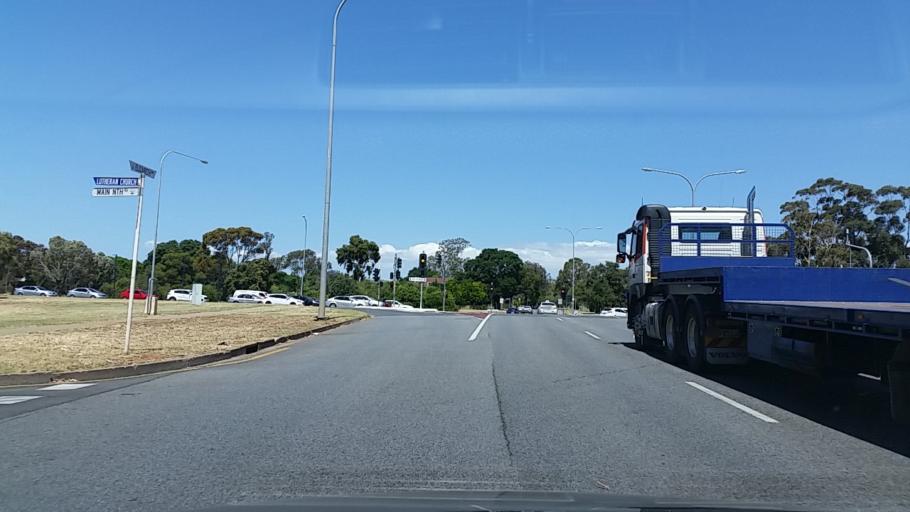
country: AU
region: South Australia
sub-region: Salisbury
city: Elizabeth
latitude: -34.7151
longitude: 138.6726
